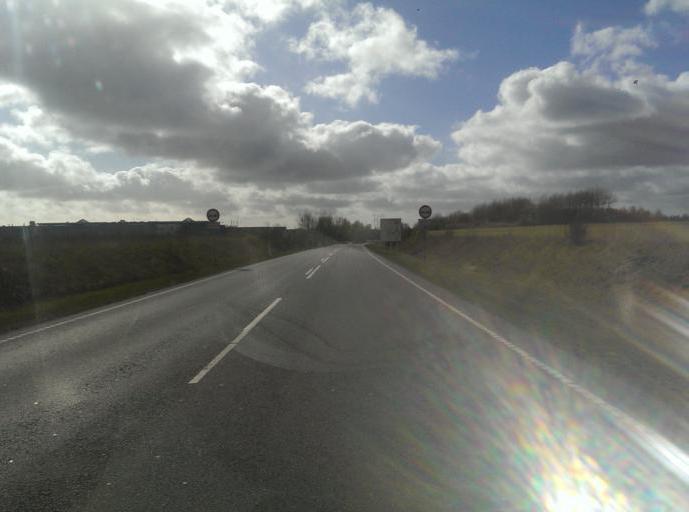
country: DK
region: South Denmark
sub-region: Esbjerg Kommune
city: Esbjerg
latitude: 55.5170
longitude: 8.4738
